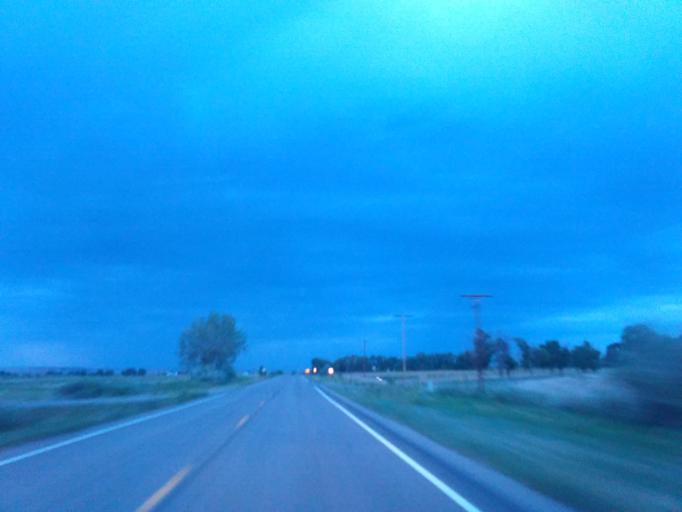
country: US
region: Colorado
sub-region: Las Animas County
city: Trinidad
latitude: 37.2628
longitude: -104.3583
